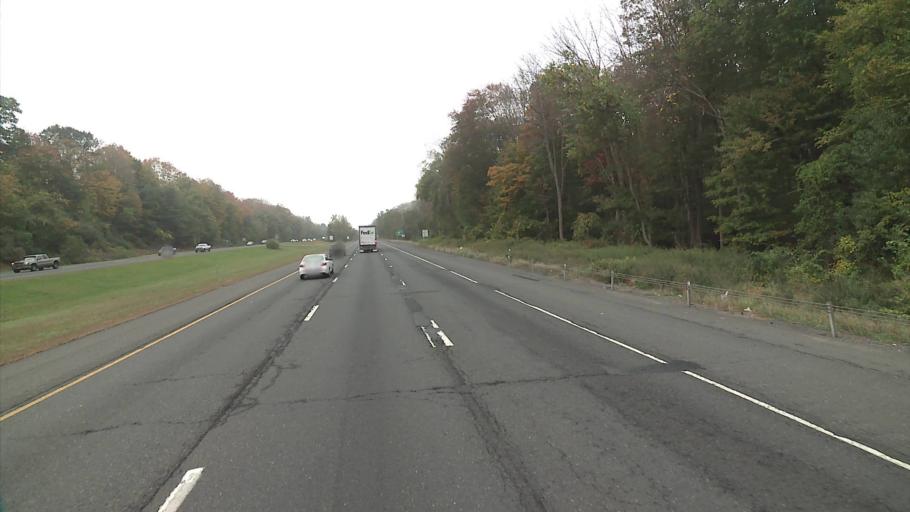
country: US
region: Connecticut
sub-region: Fairfield County
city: Newtown
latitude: 41.4292
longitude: -73.2520
